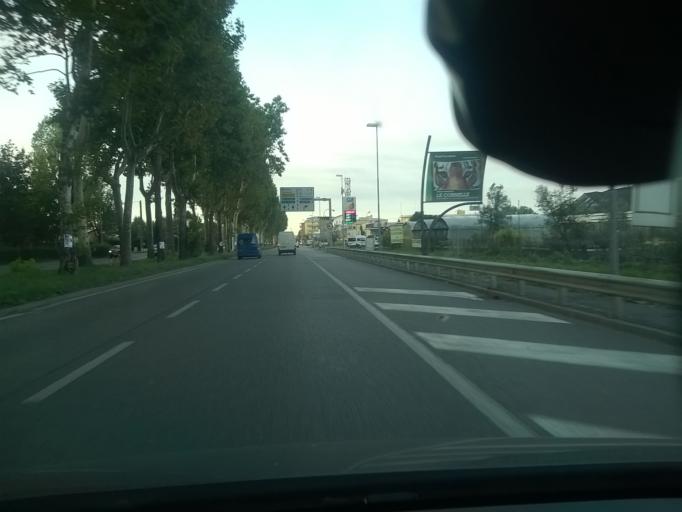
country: IT
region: Lombardy
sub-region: Provincia di Bergamo
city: Gorle
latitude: 45.6987
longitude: 9.6954
